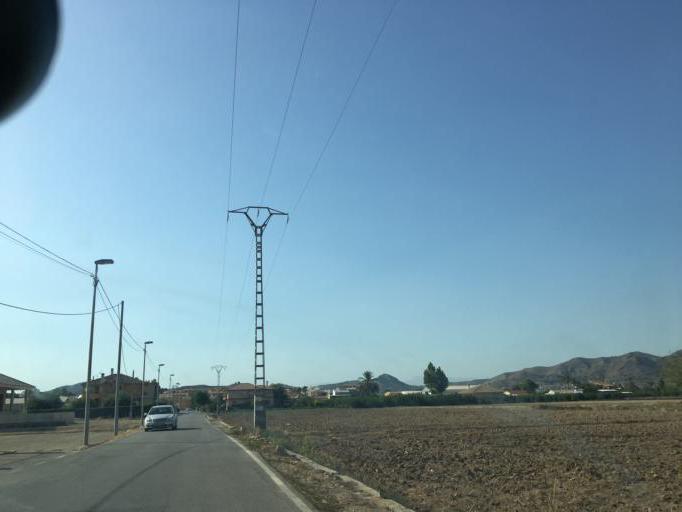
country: ES
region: Murcia
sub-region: Murcia
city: Santomera
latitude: 38.0340
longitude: -1.0720
